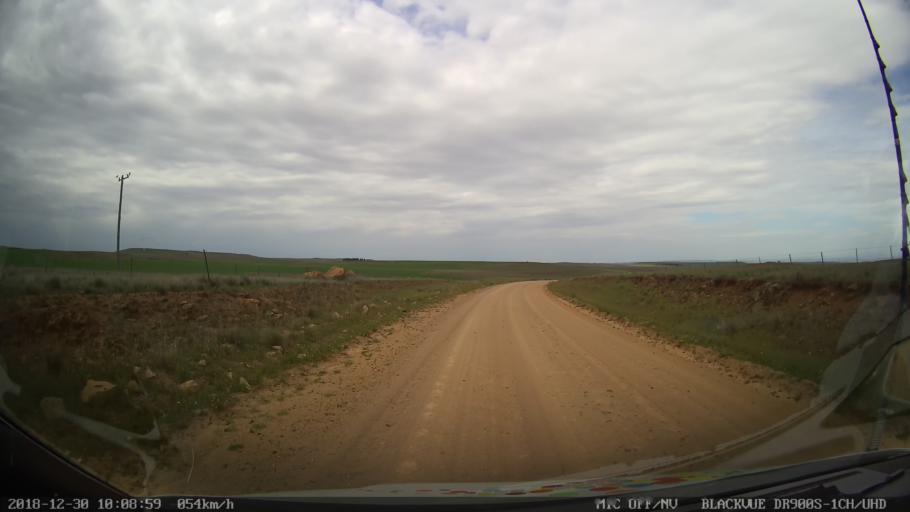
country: AU
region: New South Wales
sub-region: Cooma-Monaro
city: Cooma
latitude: -36.5470
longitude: 149.1090
